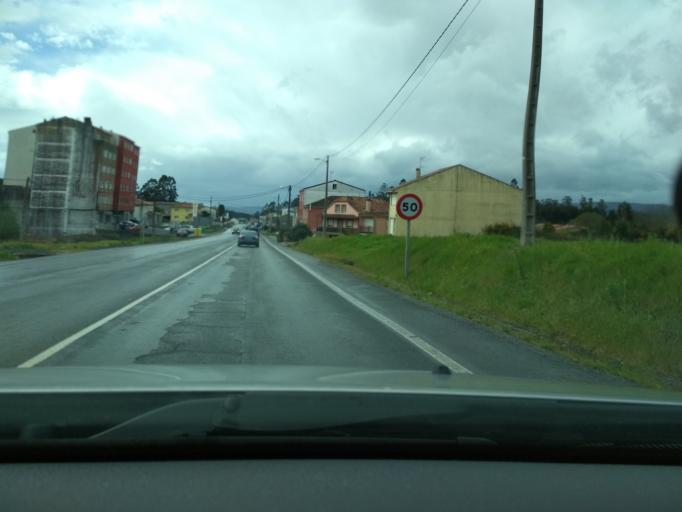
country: ES
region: Galicia
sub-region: Provincia da Coruna
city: Santiago de Compostela
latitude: 42.8378
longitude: -8.5846
